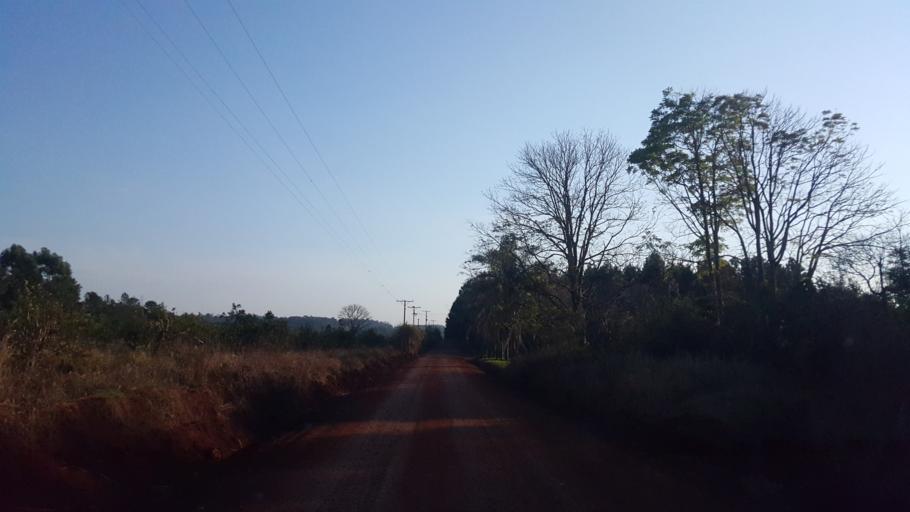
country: AR
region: Misiones
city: Capiovi
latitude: -26.9059
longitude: -55.0505
